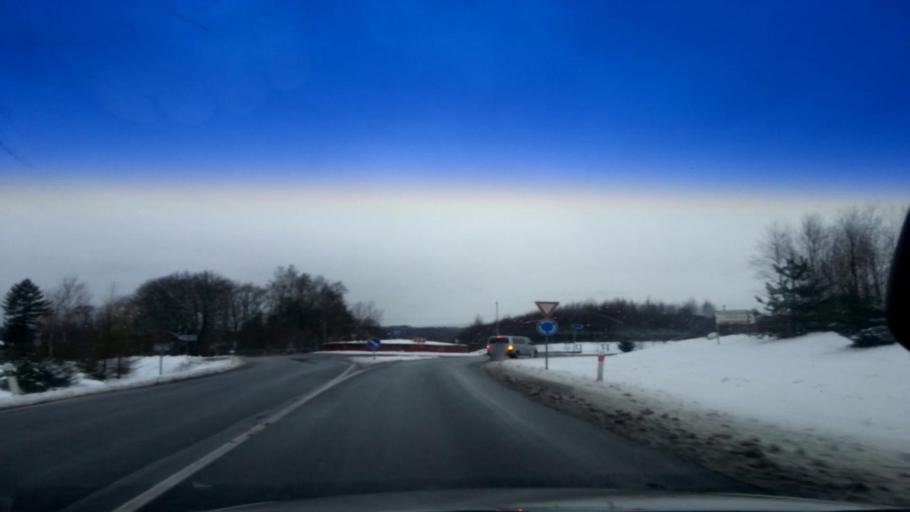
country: CZ
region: Karlovarsky
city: As
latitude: 50.1936
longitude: 12.2171
